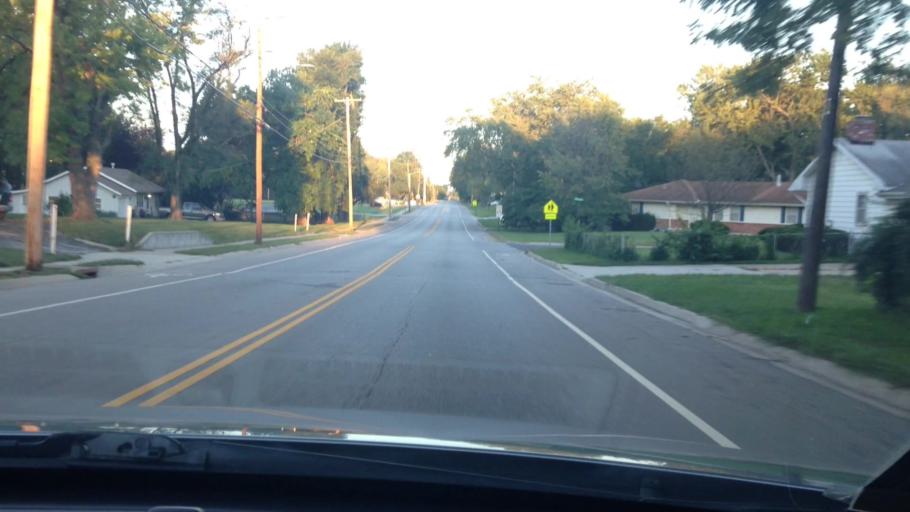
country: US
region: Missouri
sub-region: Jackson County
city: Raytown
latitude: 38.9732
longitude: -94.4828
